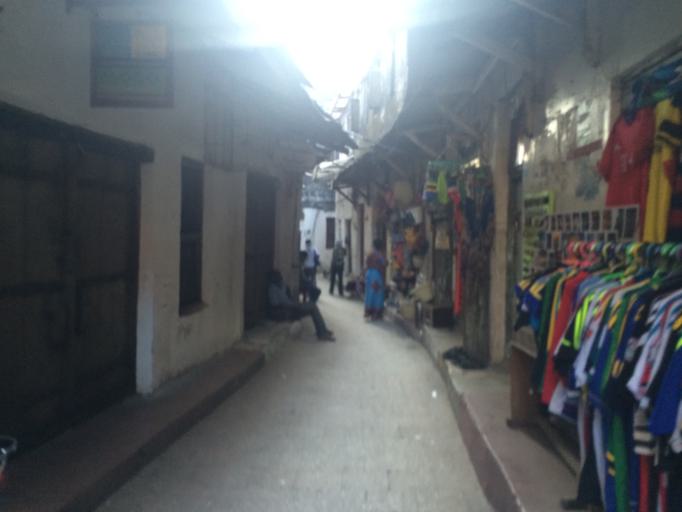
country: TZ
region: Zanzibar Urban/West
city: Zanzibar
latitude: -6.1614
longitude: 39.1904
